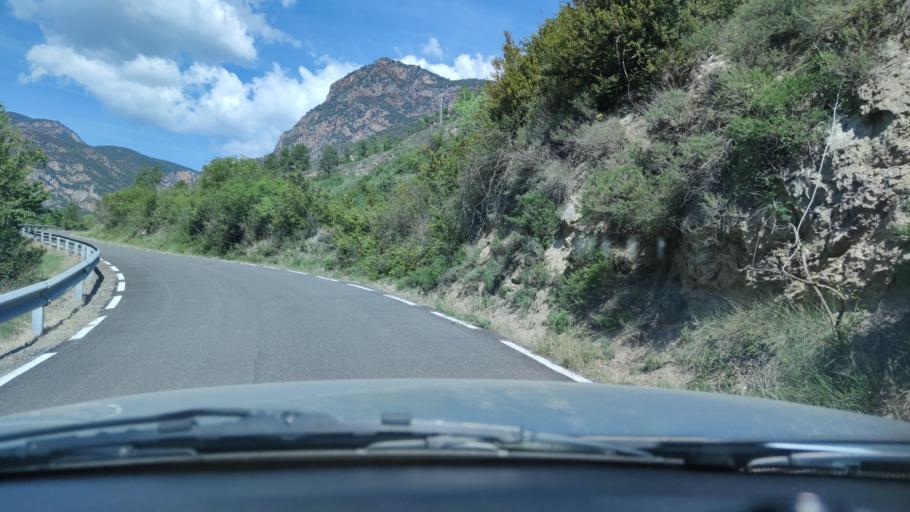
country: ES
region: Catalonia
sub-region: Provincia de Lleida
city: Coll de Nargo
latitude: 42.2925
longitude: 1.3221
